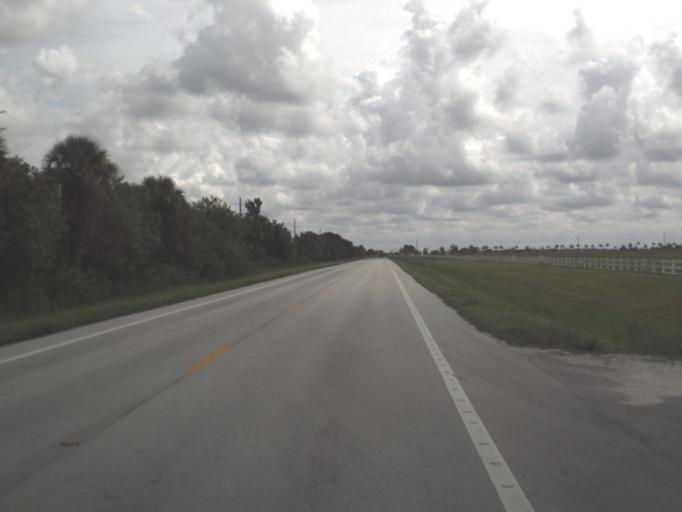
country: US
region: Florida
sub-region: Glades County
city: Buckhead Ridge
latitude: 27.2361
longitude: -81.0455
